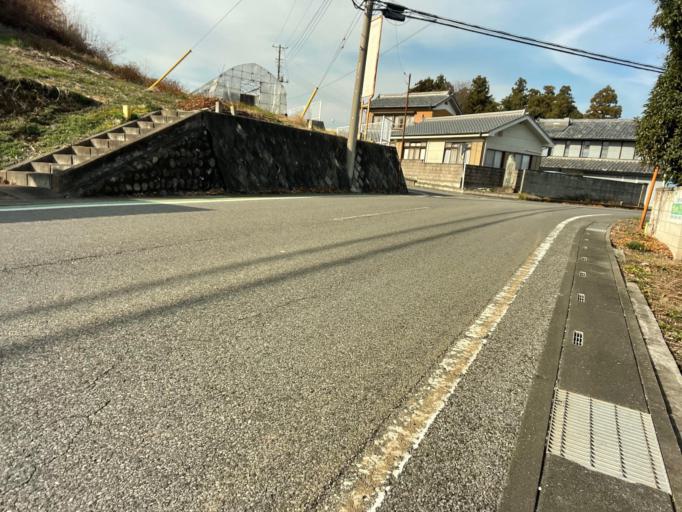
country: JP
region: Saitama
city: Yorii
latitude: 36.1602
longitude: 139.1788
